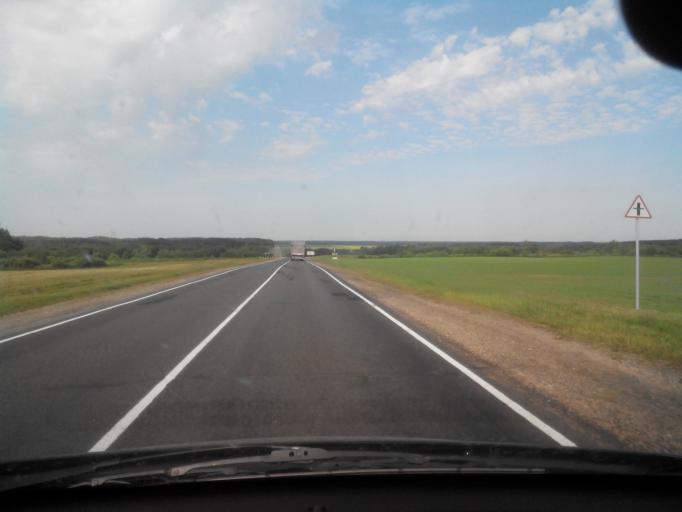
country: BY
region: Minsk
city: Myadzyel
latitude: 55.0361
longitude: 26.9912
